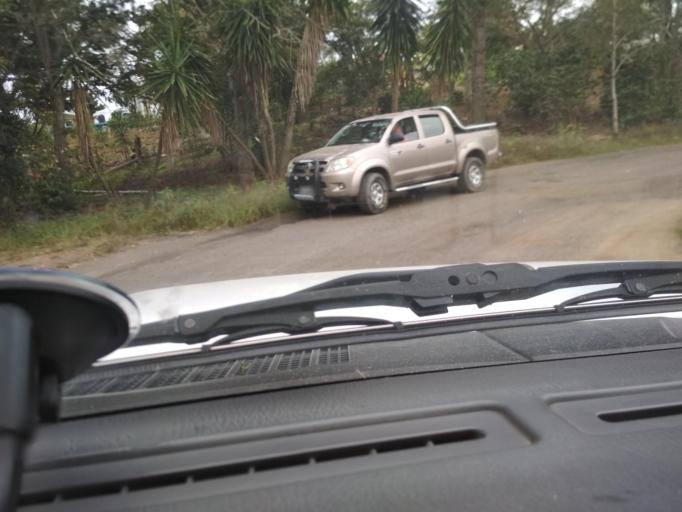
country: MX
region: Veracruz
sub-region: Emiliano Zapata
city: Dos Rios
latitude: 19.5346
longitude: -96.8016
